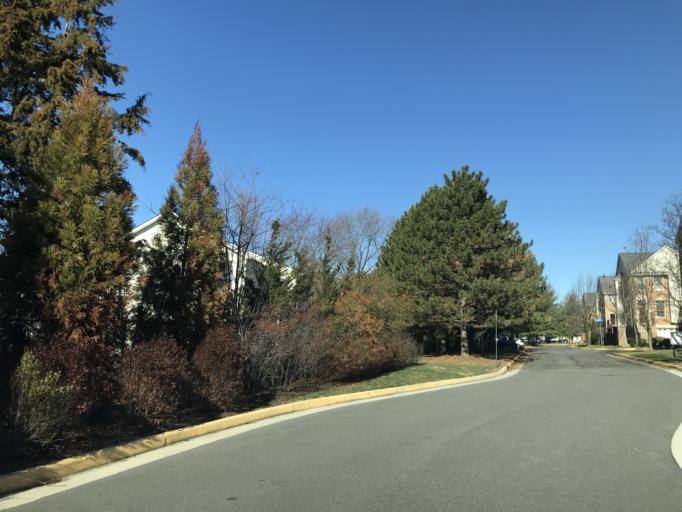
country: US
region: Virginia
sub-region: Fairfax County
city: Franconia
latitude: 38.7778
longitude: -77.1544
